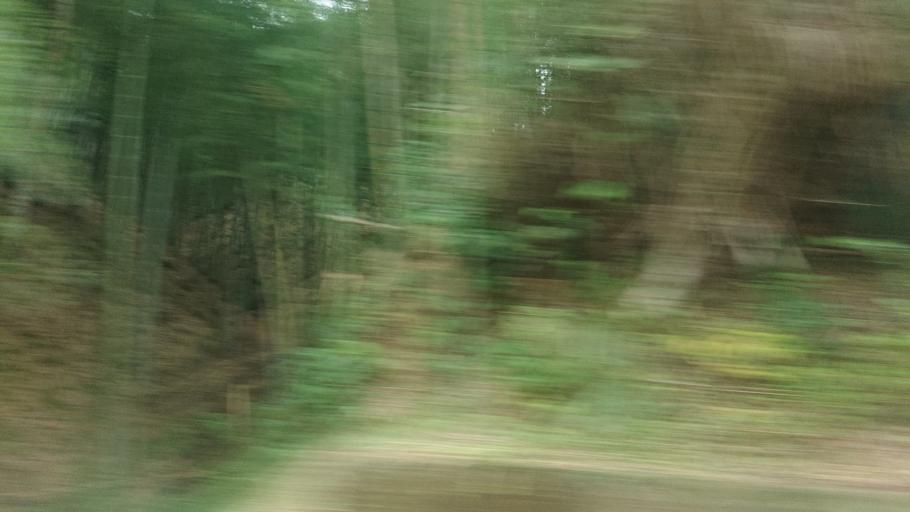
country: TW
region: Taiwan
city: Lugu
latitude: 23.6282
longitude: 120.7194
